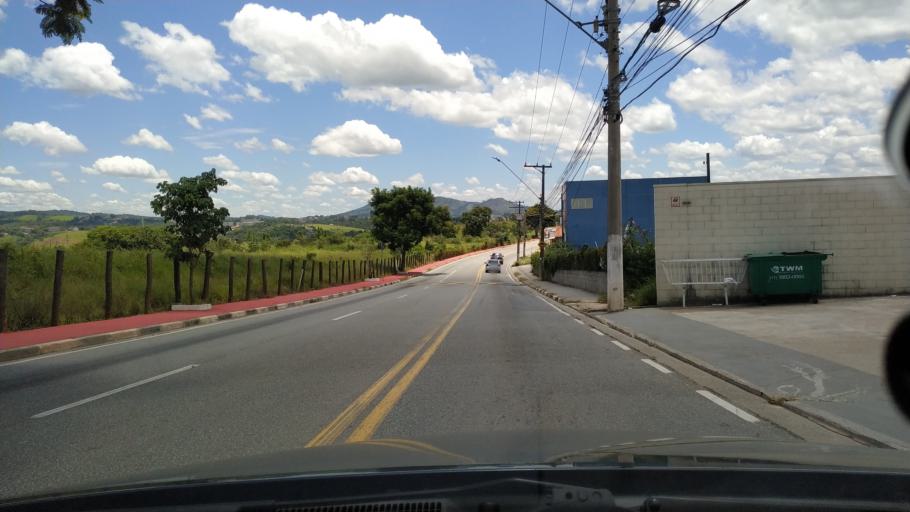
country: BR
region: Sao Paulo
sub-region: Santana De Parnaiba
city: Santana de Parnaiba
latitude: -23.4530
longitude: -46.8979
